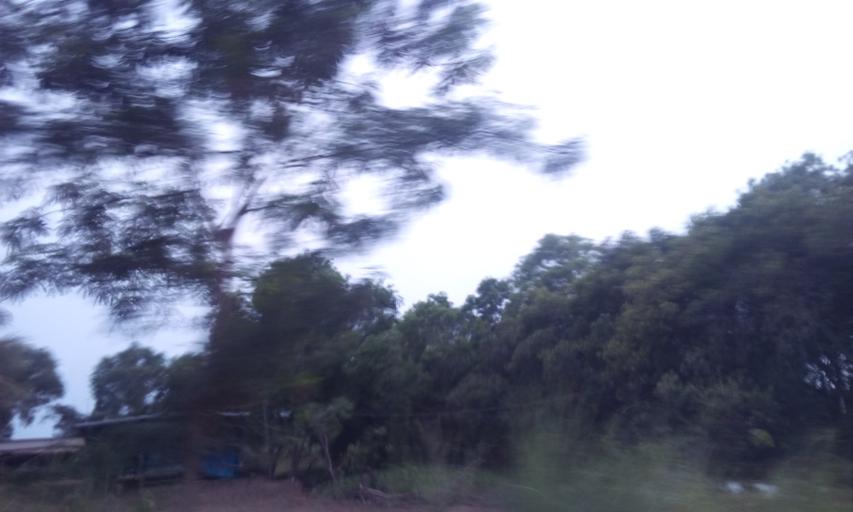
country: TH
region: Chachoengsao
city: Plaeng Yao
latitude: 13.5943
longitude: 101.1935
